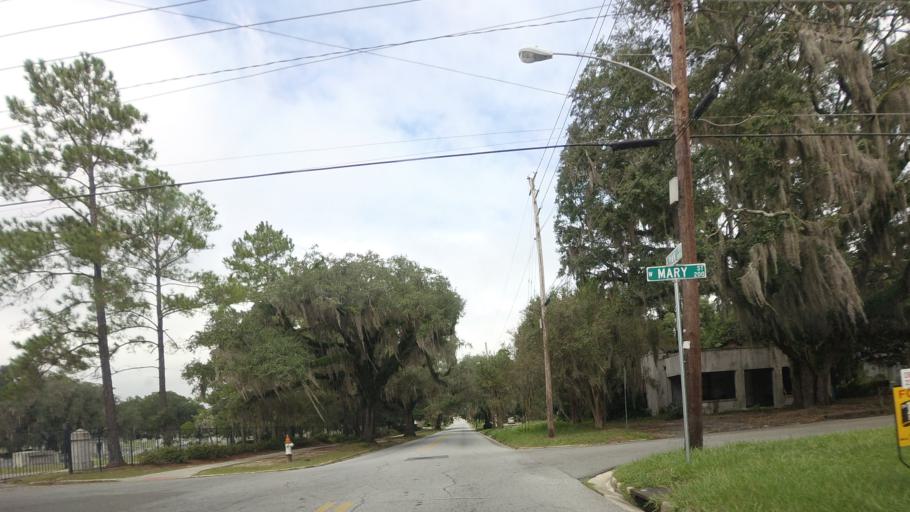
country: US
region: Georgia
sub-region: Lowndes County
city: Valdosta
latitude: 30.8407
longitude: -83.2873
